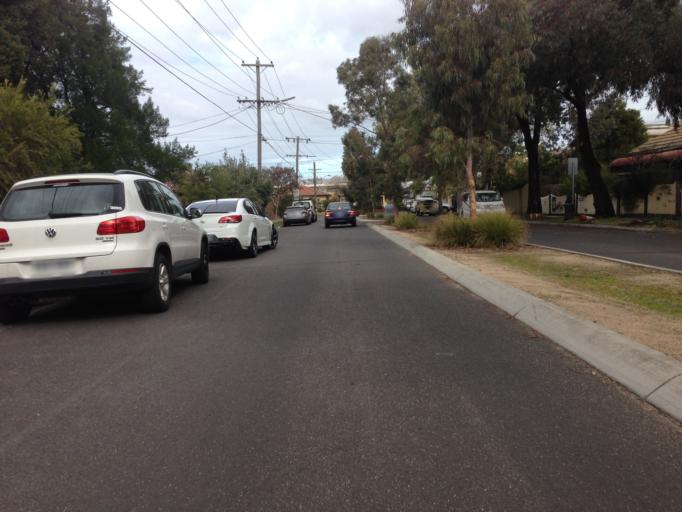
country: AU
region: Victoria
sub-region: Darebin
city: Fairfield
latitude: -37.7815
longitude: 145.0086
